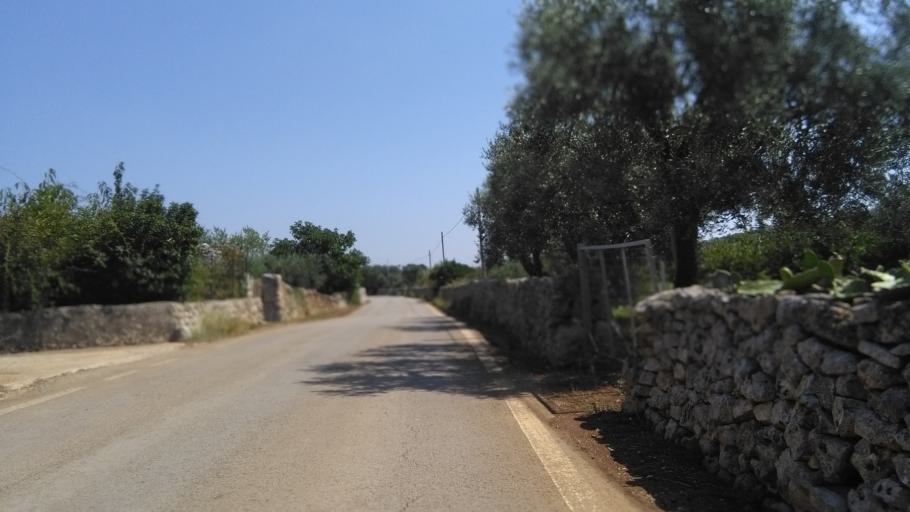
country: IT
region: Apulia
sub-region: Provincia di Bari
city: Alberobello
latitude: 40.7978
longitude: 17.2163
